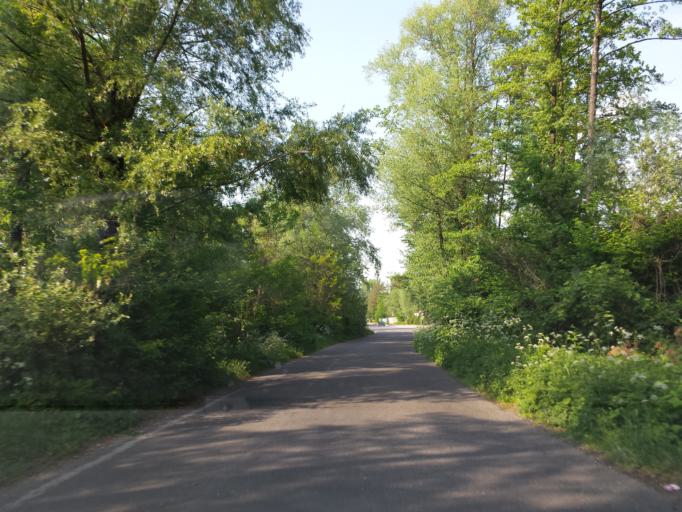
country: SK
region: Bratislavsky
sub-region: Okres Malacky
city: Malacky
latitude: 48.4126
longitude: 17.0200
